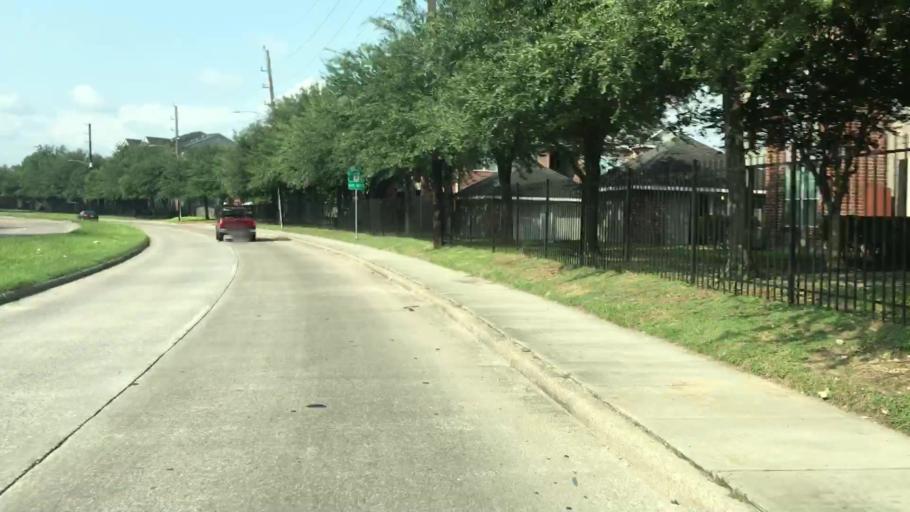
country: US
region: Texas
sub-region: Harris County
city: Aldine
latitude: 29.9342
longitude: -95.4014
